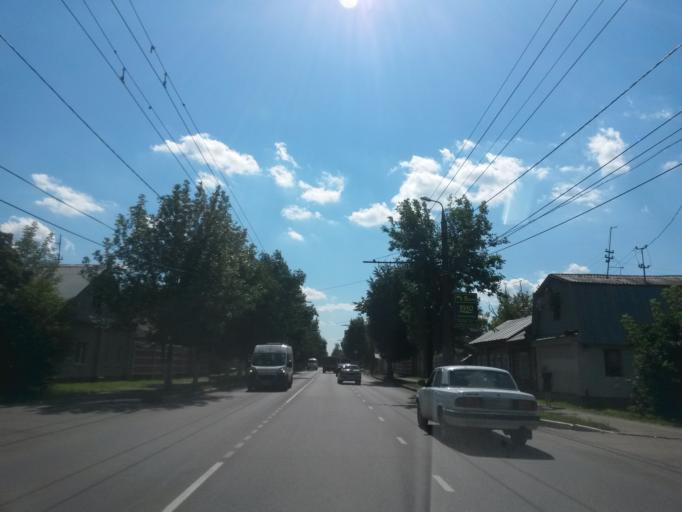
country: RU
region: Ivanovo
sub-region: Gorod Ivanovo
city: Ivanovo
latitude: 56.9904
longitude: 40.9849
